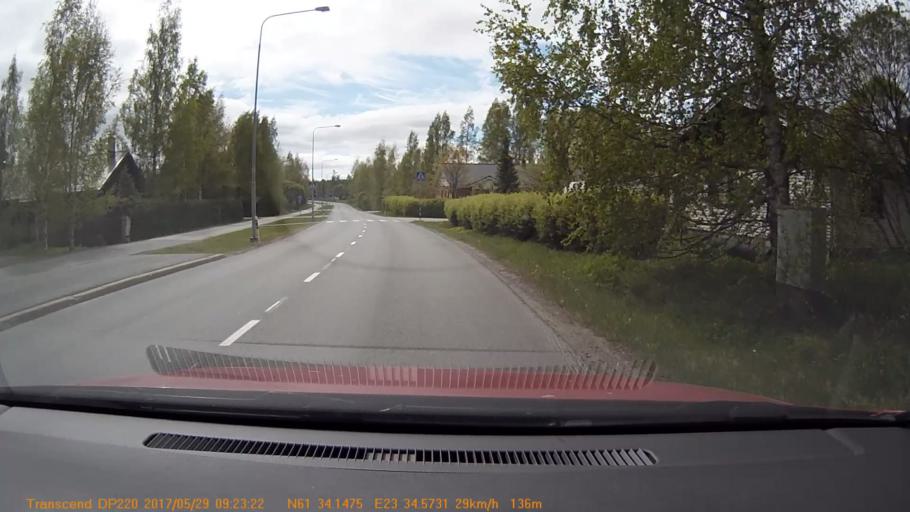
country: FI
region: Pirkanmaa
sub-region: Tampere
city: Yloejaervi
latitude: 61.5692
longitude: 23.5763
